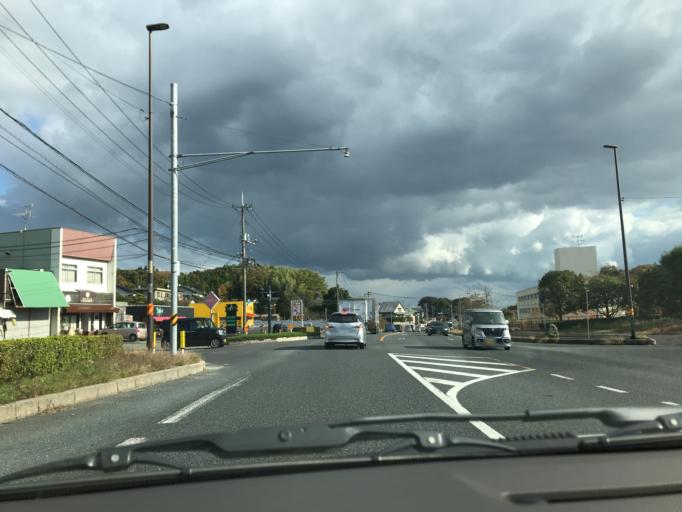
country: JP
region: Shimane
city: Yasugicho
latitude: 35.4326
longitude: 133.1622
